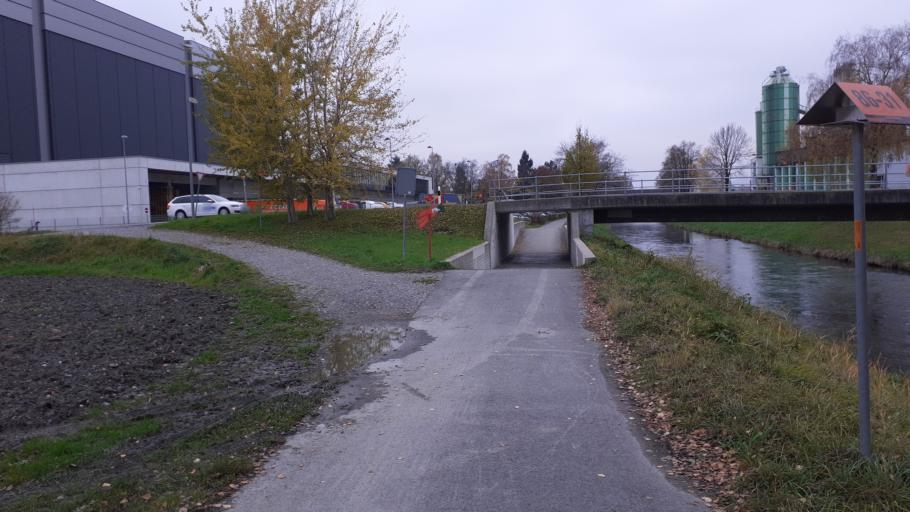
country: CH
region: Saint Gallen
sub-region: Wahlkreis Rheintal
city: Au
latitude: 47.4163
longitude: 9.6409
